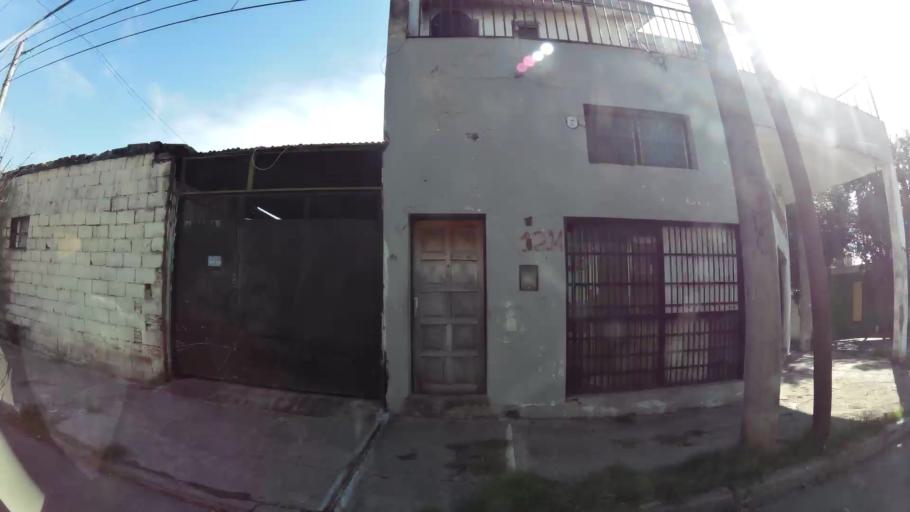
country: AR
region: Cordoba
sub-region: Departamento de Capital
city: Cordoba
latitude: -31.4406
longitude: -64.2101
